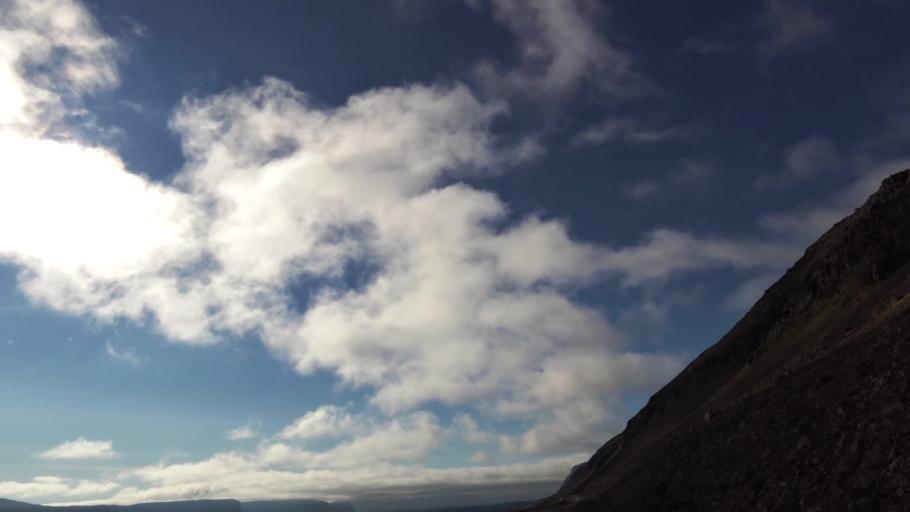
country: IS
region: West
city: Olafsvik
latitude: 65.5610
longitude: -23.9100
